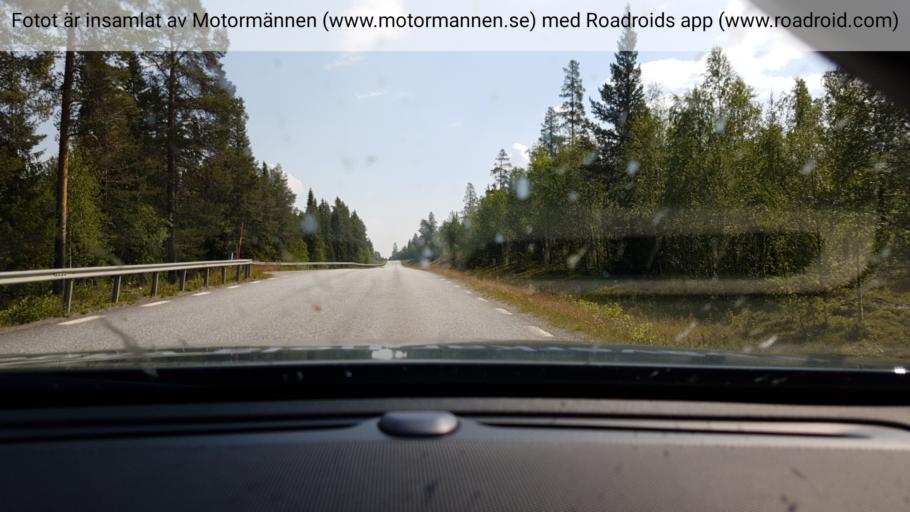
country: SE
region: Vaesterbotten
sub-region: Storumans Kommun
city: Fristad
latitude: 65.4034
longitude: 16.3646
